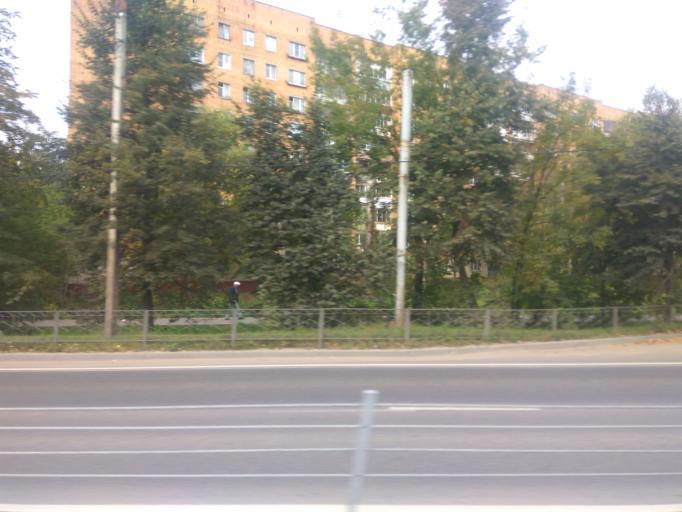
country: RU
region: Moskovskaya
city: Fryazino
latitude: 55.9493
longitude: 38.0477
